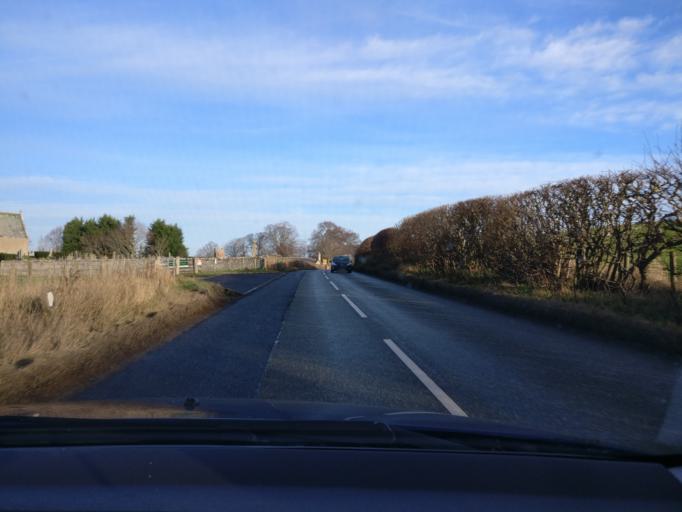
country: GB
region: Scotland
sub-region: The Scottish Borders
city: Kelso
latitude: 55.5353
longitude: -2.4667
